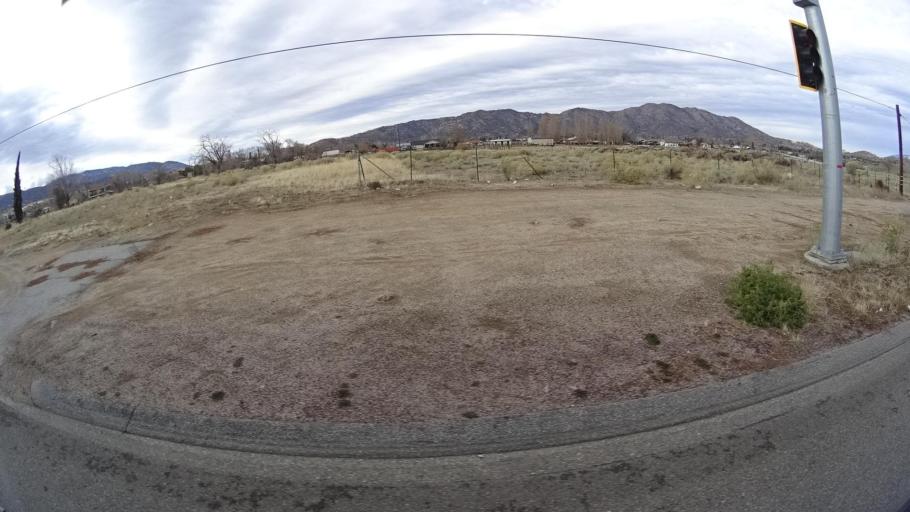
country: US
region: California
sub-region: Kern County
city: Tehachapi
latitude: 35.1297
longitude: -118.4676
